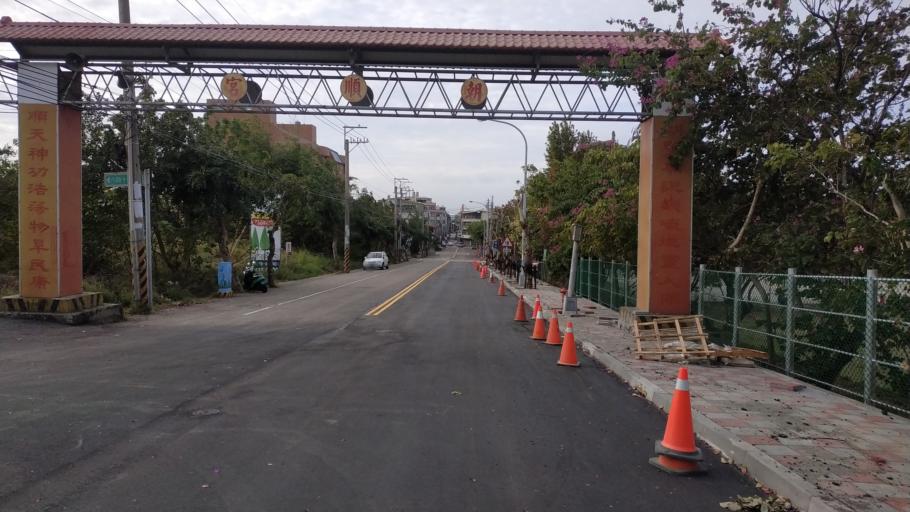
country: TW
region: Taiwan
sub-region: Taichung City
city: Taichung
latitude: 24.2156
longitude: 120.5735
